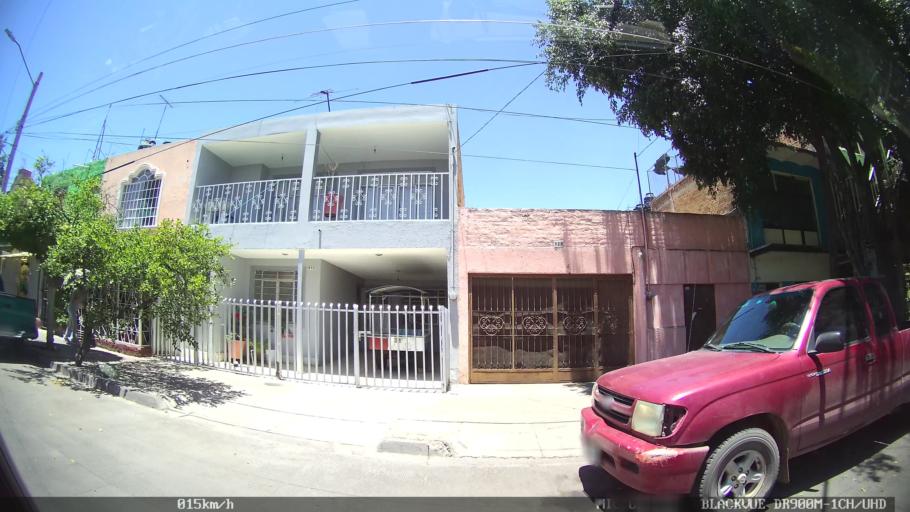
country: MX
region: Jalisco
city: Tlaquepaque
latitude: 20.6675
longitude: -103.2804
